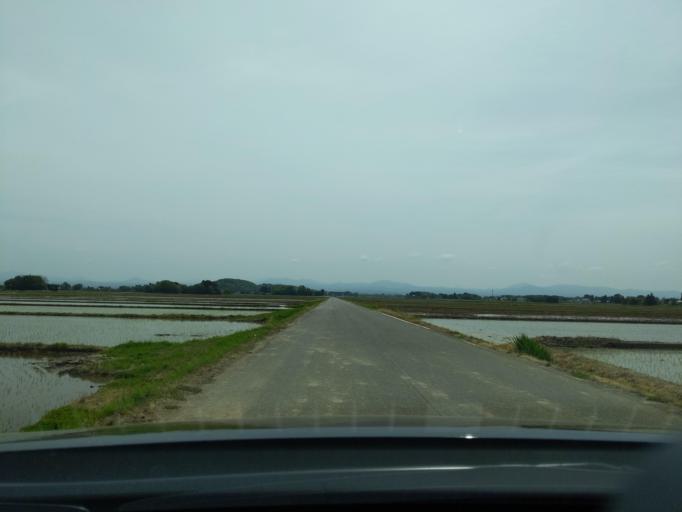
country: JP
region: Fukushima
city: Koriyama
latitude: 37.3992
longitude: 140.2748
